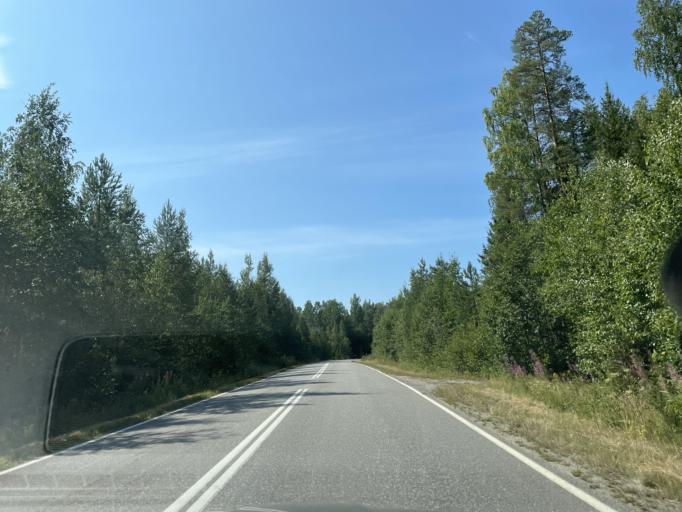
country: FI
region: Central Finland
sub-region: Saarijaervi-Viitasaari
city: Pihtipudas
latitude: 63.3630
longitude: 25.7272
